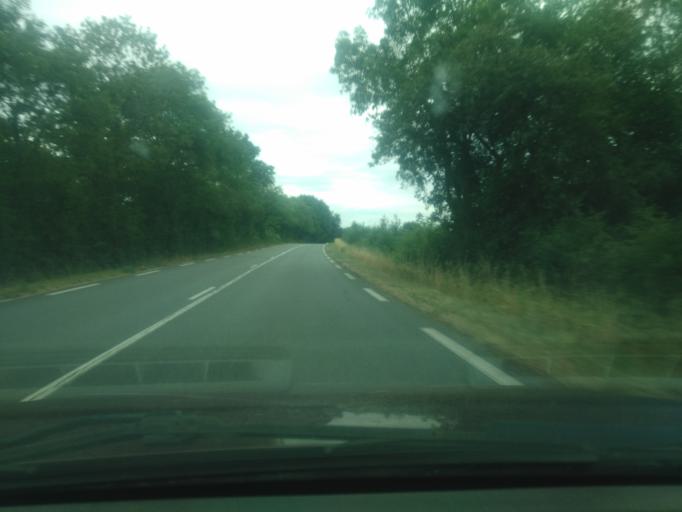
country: FR
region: Auvergne
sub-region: Departement de l'Allier
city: Ainay-le-Chateau
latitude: 46.7395
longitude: 2.6996
